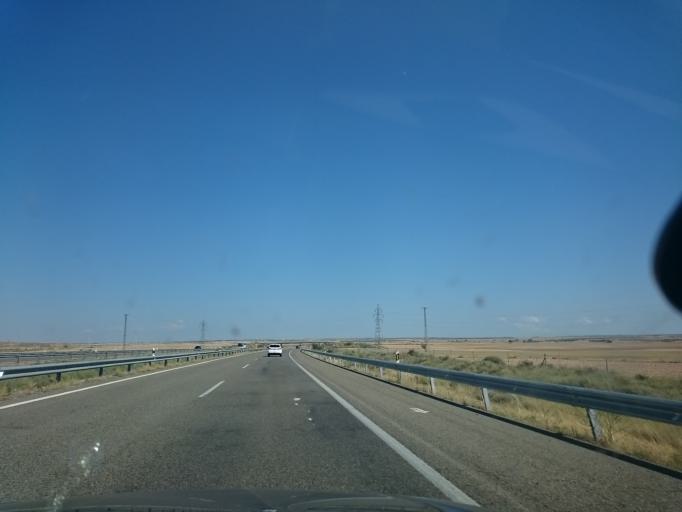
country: ES
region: Aragon
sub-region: Provincia de Huesca
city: Candasnos
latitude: 41.4848
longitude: 0.1789
